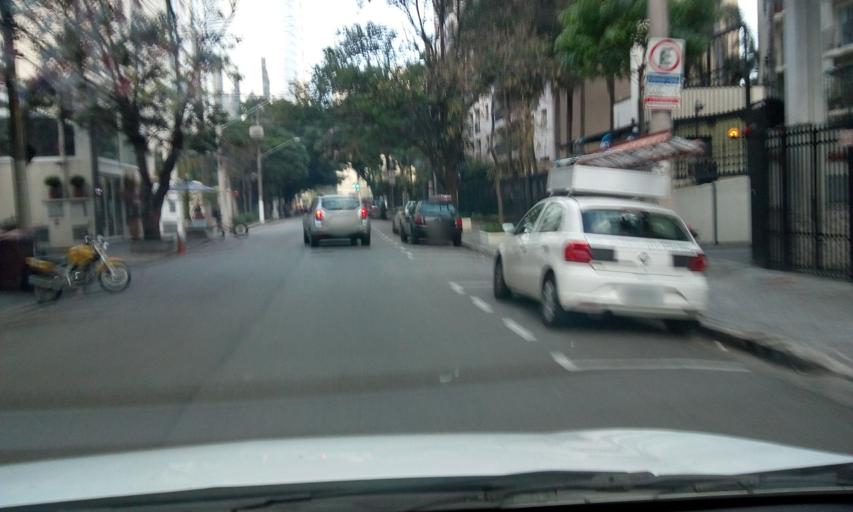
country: BR
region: Sao Paulo
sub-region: Sao Paulo
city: Sao Paulo
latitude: -23.5747
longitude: -46.6586
